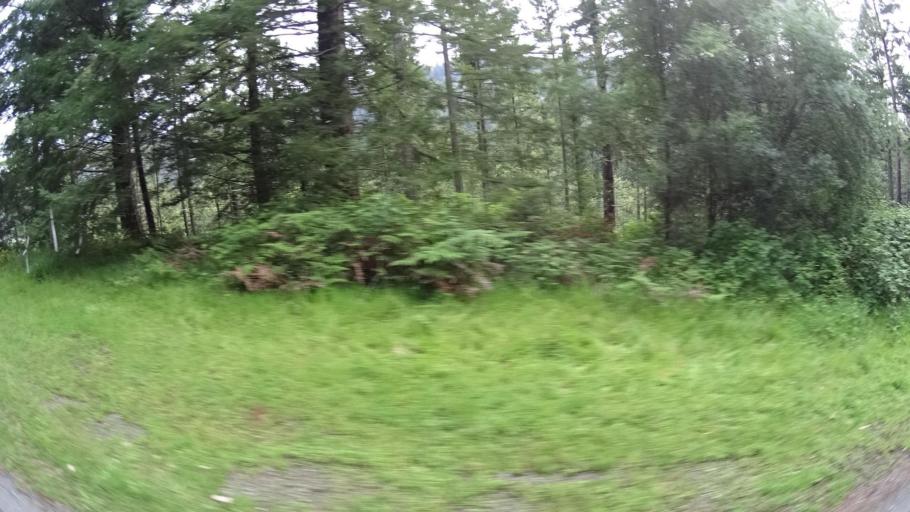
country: US
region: California
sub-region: Humboldt County
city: Redway
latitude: 40.3344
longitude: -123.8507
